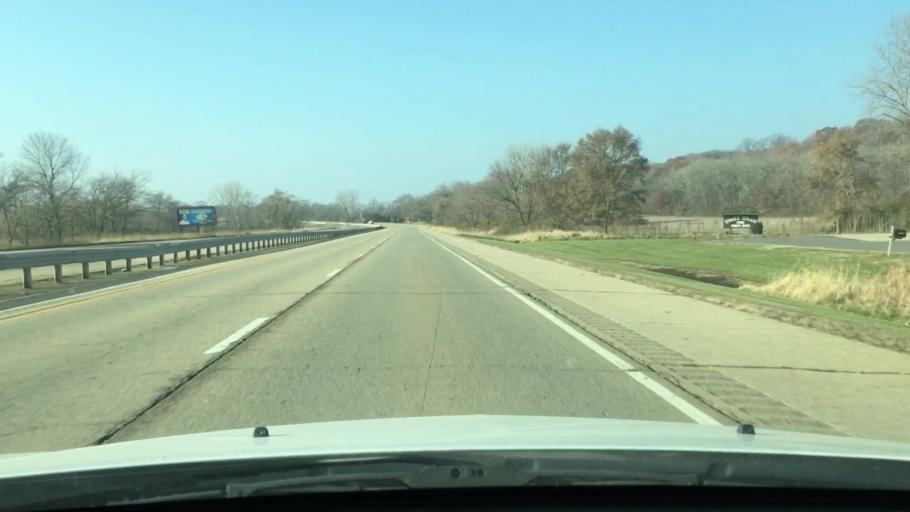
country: US
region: Illinois
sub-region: Tazewell County
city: Pekin
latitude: 40.5753
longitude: -89.7095
